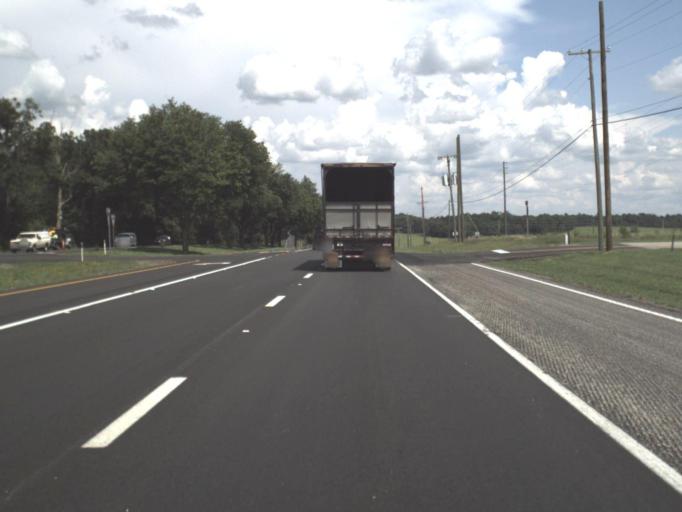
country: US
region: Florida
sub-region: Alachua County
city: Alachua
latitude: 29.7792
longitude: -82.4522
